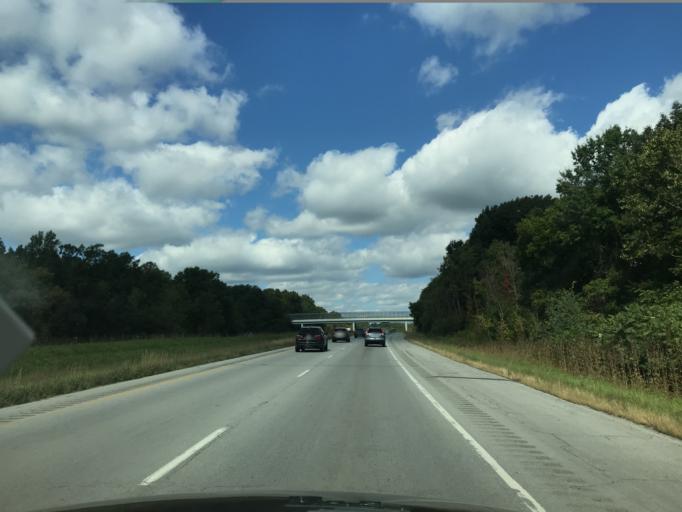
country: US
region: Ohio
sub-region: Summit County
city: Twinsburg
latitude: 41.3254
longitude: -81.4732
